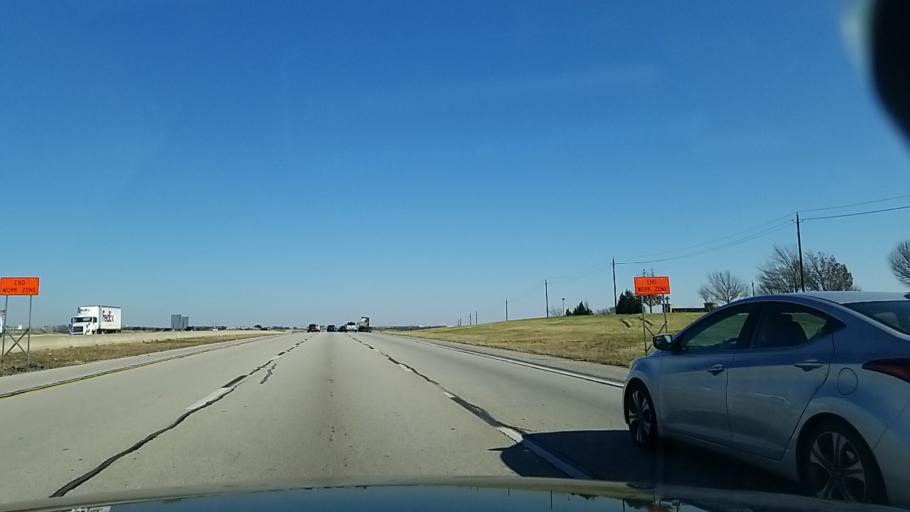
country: US
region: Texas
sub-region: Tarrant County
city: Sansom Park
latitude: 32.8195
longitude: -97.4003
